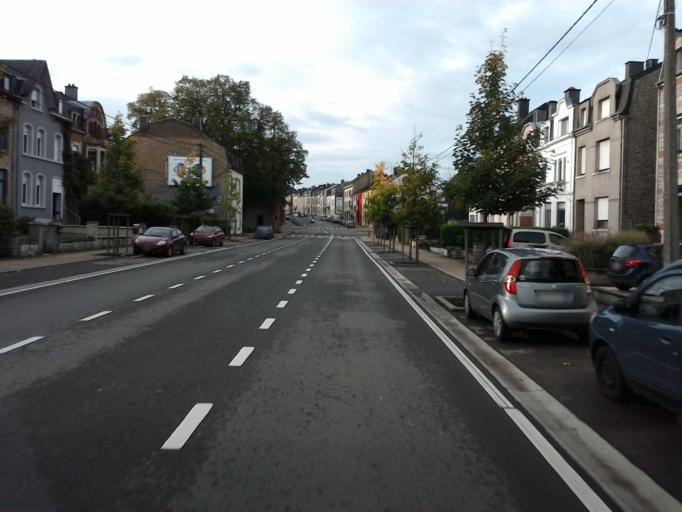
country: BE
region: Wallonia
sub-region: Province du Luxembourg
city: Arlon
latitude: 49.6907
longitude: 5.8112
